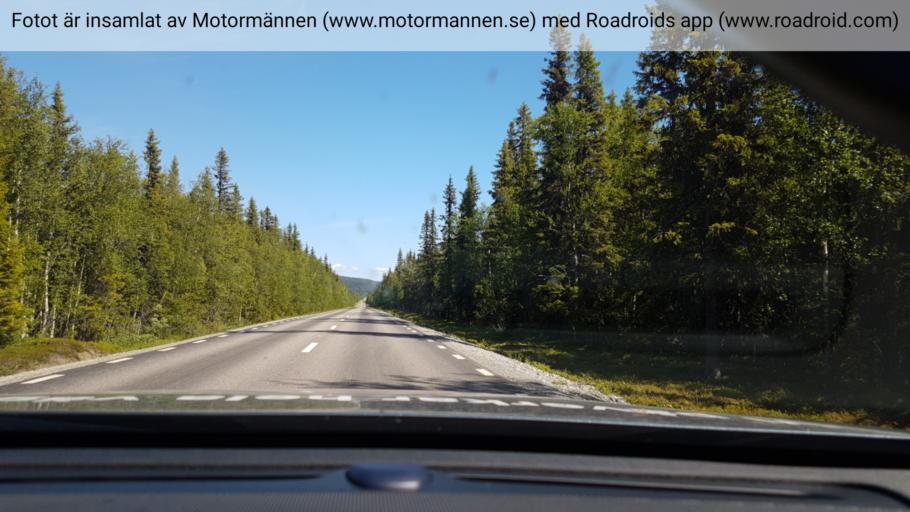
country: SE
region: Vaesterbotten
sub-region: Asele Kommun
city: Insjon
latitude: 64.7263
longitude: 17.5783
